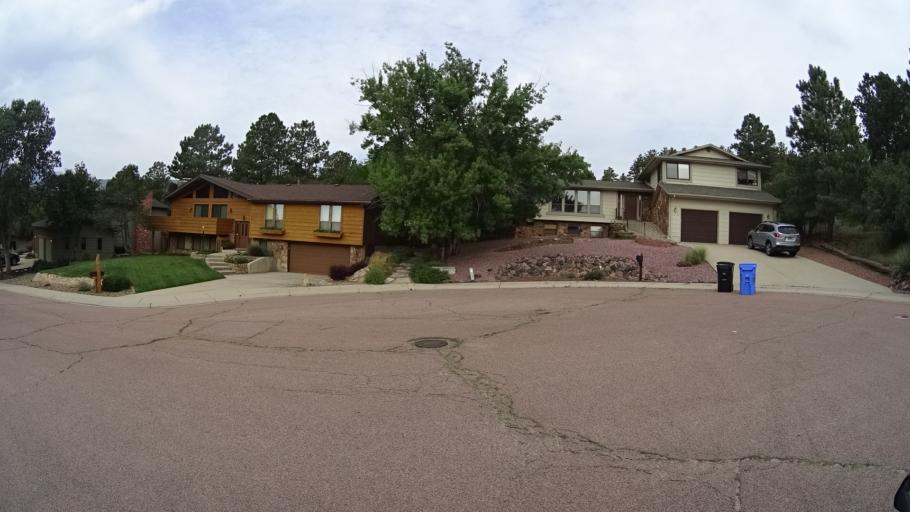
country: US
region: Colorado
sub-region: El Paso County
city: Air Force Academy
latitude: 38.9316
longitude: -104.8376
